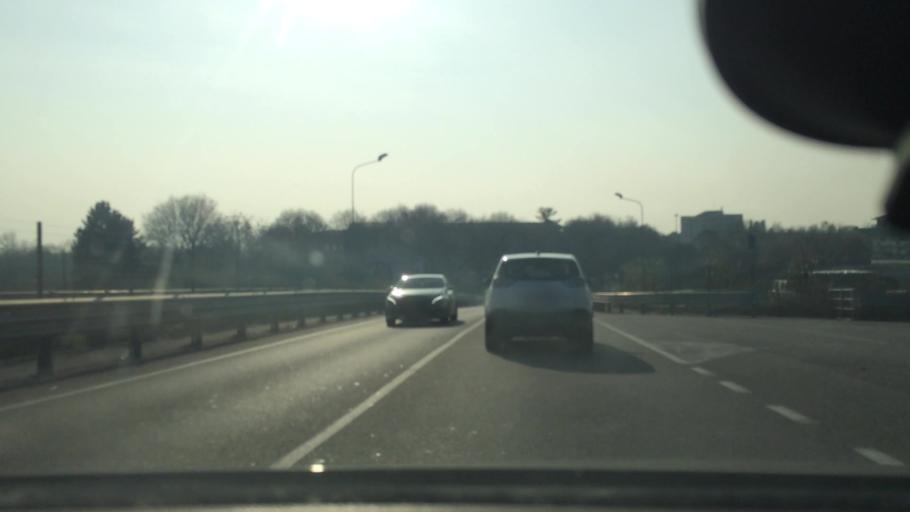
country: IT
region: Lombardy
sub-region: Citta metropolitana di Milano
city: Passirana
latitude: 45.5517
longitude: 9.0521
